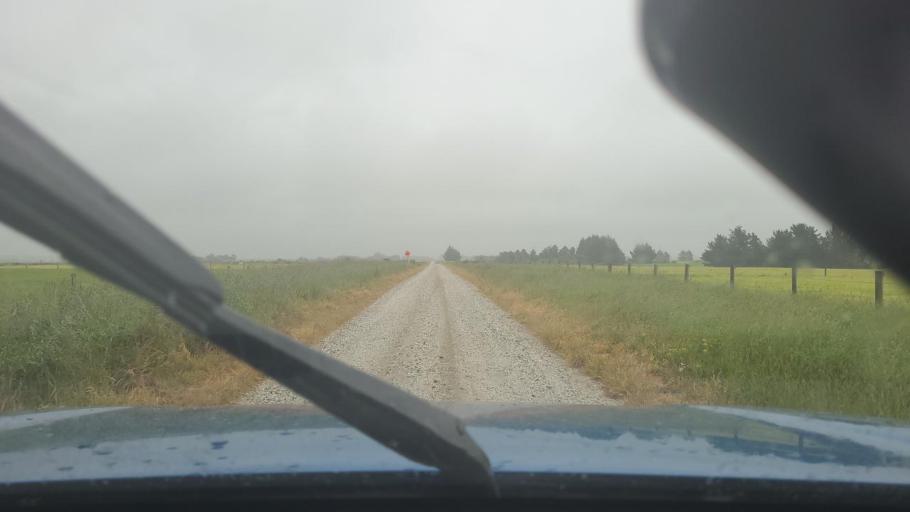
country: NZ
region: Southland
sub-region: Invercargill City
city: Invercargill
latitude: -46.4222
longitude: 168.7184
